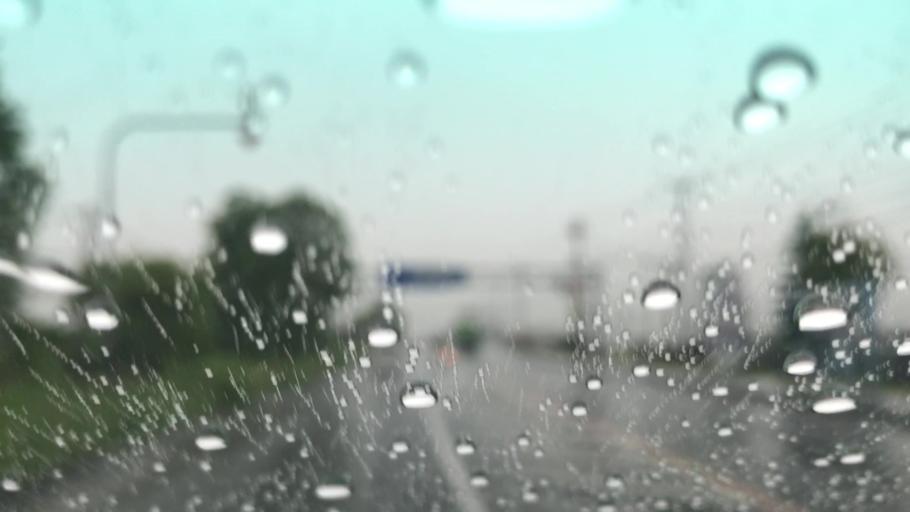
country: JP
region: Hokkaido
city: Nayoro
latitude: 44.2874
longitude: 142.4156
